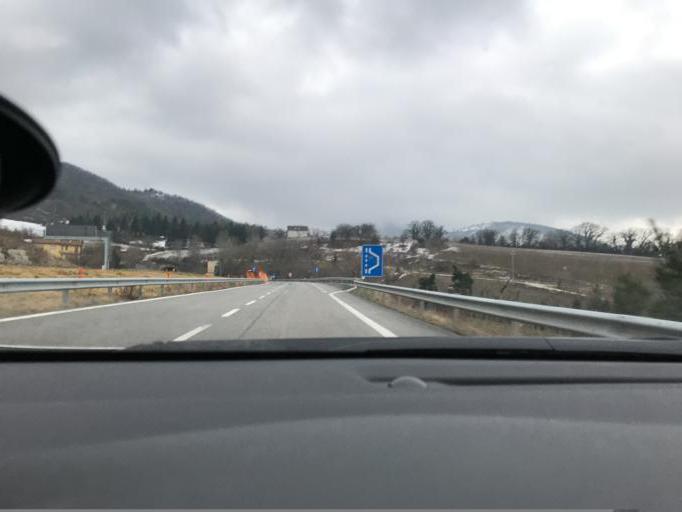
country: IT
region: The Marches
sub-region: Provincia di Ancona
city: Fabriano
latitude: 43.3253
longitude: 12.9086
